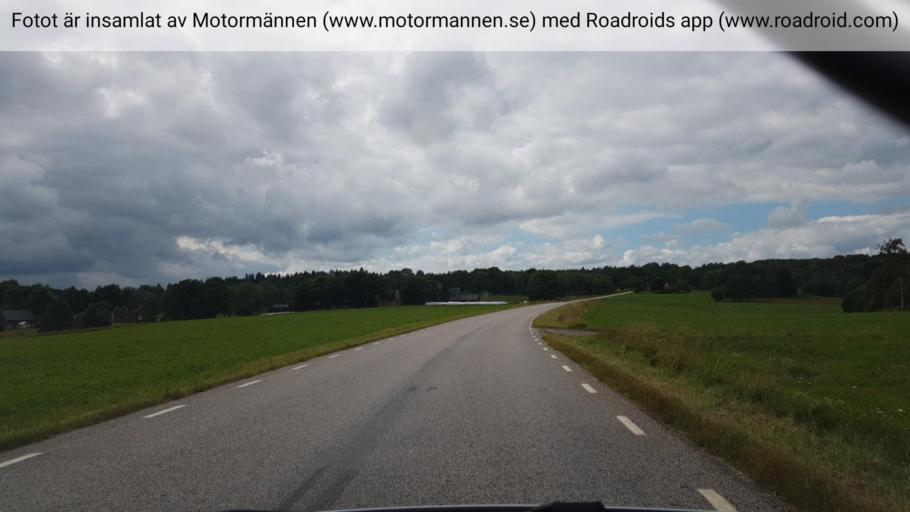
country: SE
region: Vaestra Goetaland
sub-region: Ulricehamns Kommun
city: Ulricehamn
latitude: 57.7997
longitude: 13.5907
